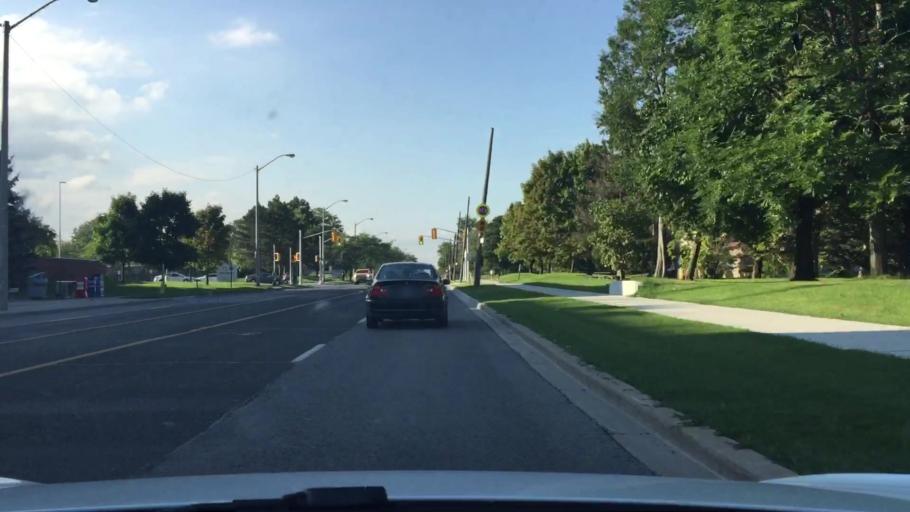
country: CA
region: Ontario
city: Scarborough
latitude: 43.8019
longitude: -79.3080
